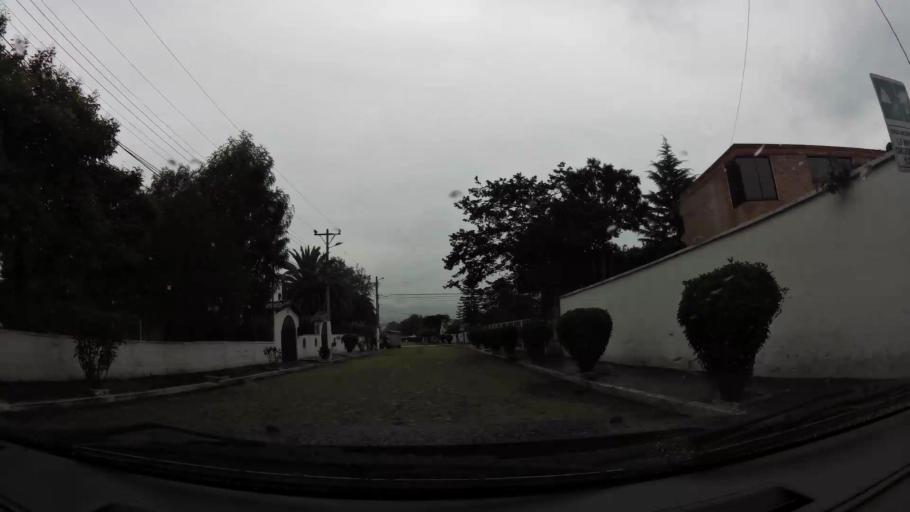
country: EC
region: Pichincha
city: Sangolqui
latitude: -0.3054
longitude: -78.4485
